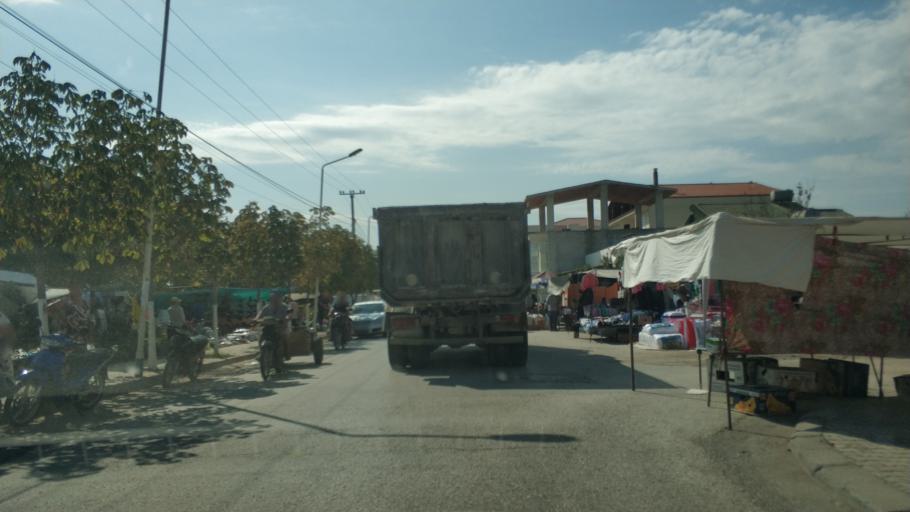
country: AL
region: Fier
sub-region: Rrethi i Lushnjes
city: Divjake
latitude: 40.9939
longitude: 19.5333
